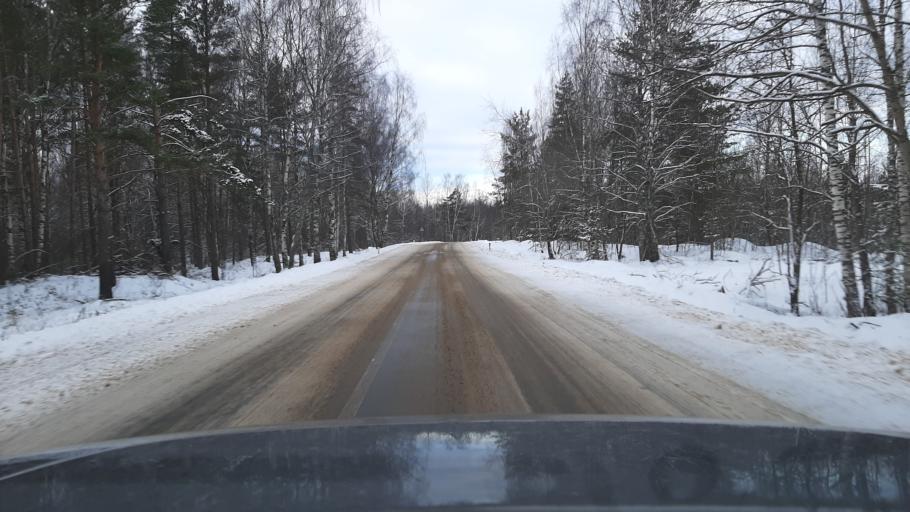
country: RU
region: Kostroma
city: Nerekhta
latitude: 57.4701
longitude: 40.6360
